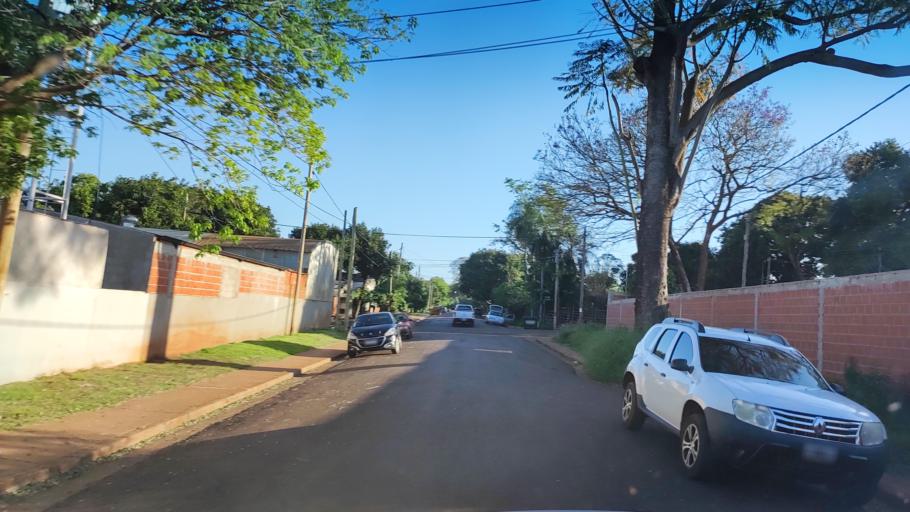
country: AR
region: Misiones
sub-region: Departamento de Capital
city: Posadas
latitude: -27.3808
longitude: -55.9355
